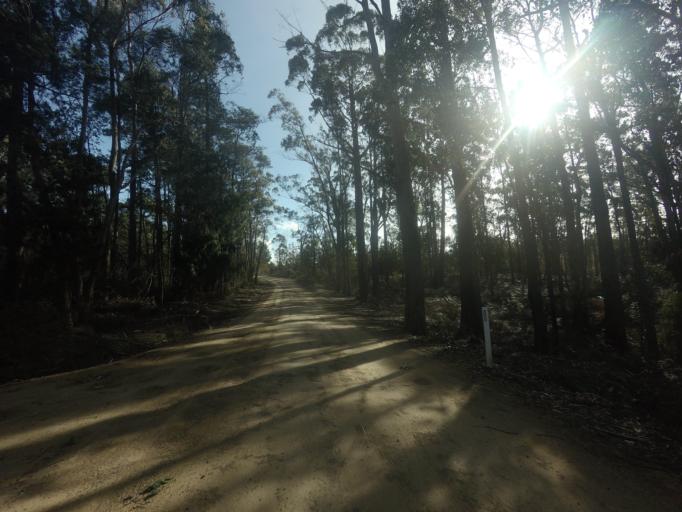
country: AU
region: Tasmania
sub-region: Kingborough
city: Kettering
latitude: -43.1124
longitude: 147.2622
